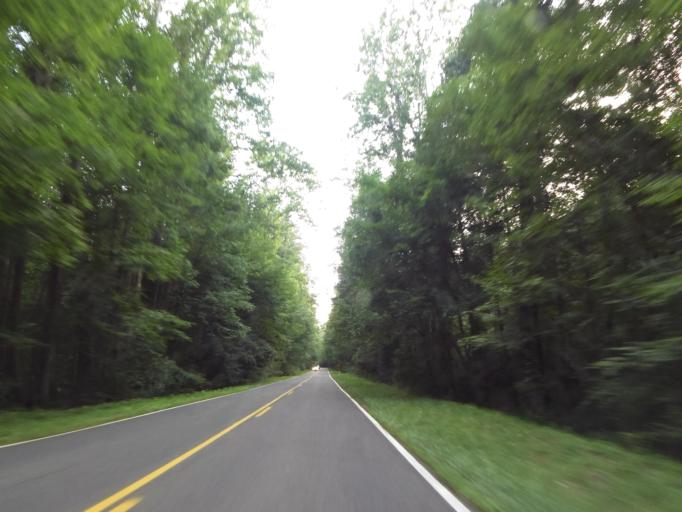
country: US
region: Tennessee
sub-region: Johnson County
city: Mountain City
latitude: 36.6193
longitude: -81.7945
